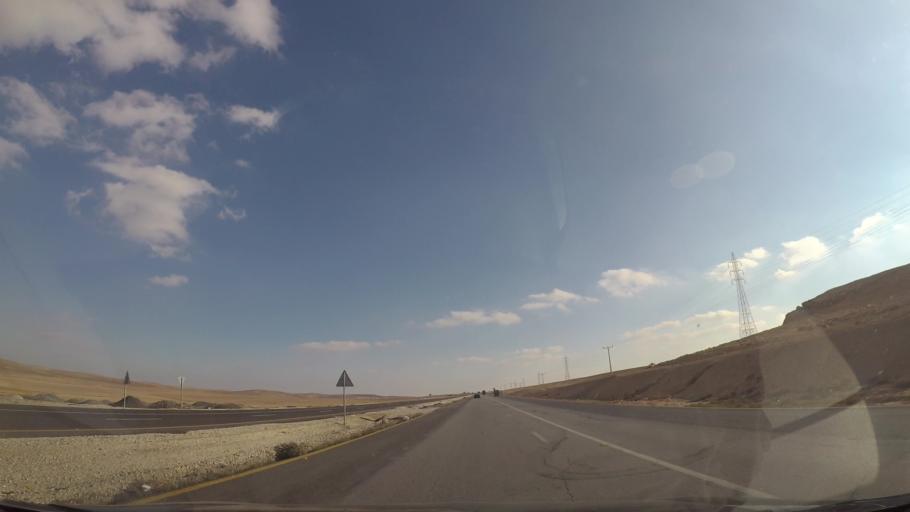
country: JO
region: Karak
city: Karak City
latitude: 31.1553
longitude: 36.0240
